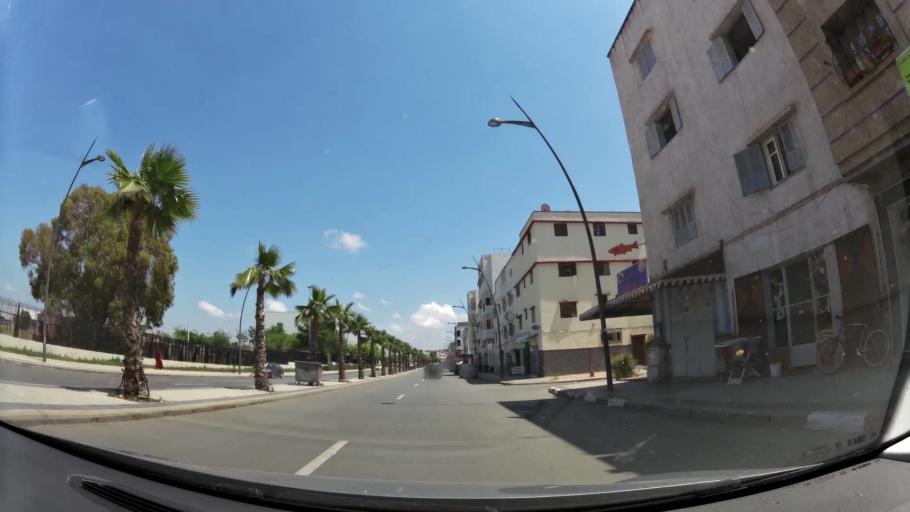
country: MA
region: Rabat-Sale-Zemmour-Zaer
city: Sale
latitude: 34.0505
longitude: -6.7969
